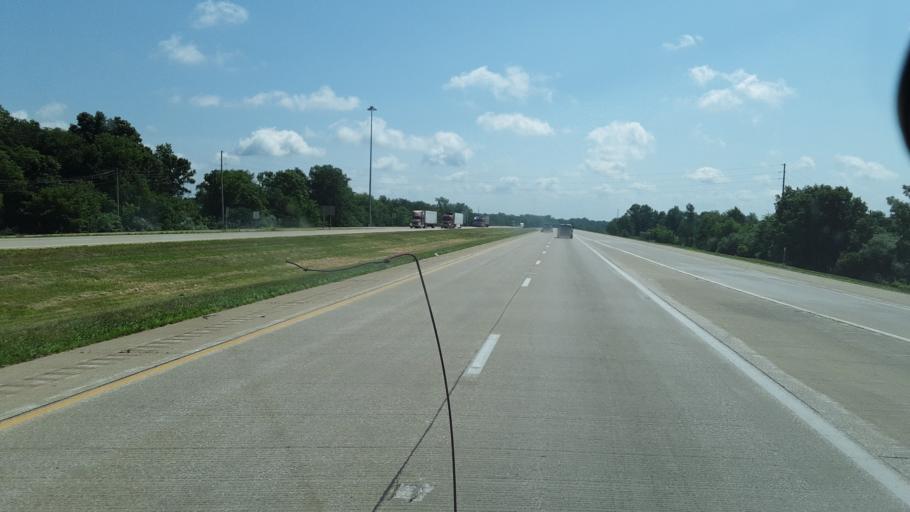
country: US
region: Illinois
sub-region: Clark County
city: Marshall
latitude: 39.4218
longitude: -87.6906
